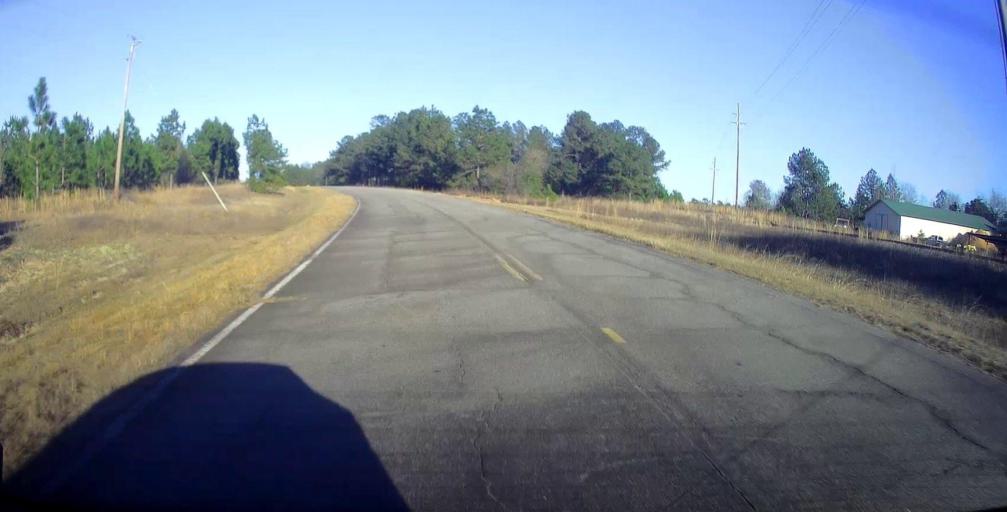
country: US
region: Georgia
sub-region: Talbot County
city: Talbotton
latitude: 32.5773
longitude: -84.5351
